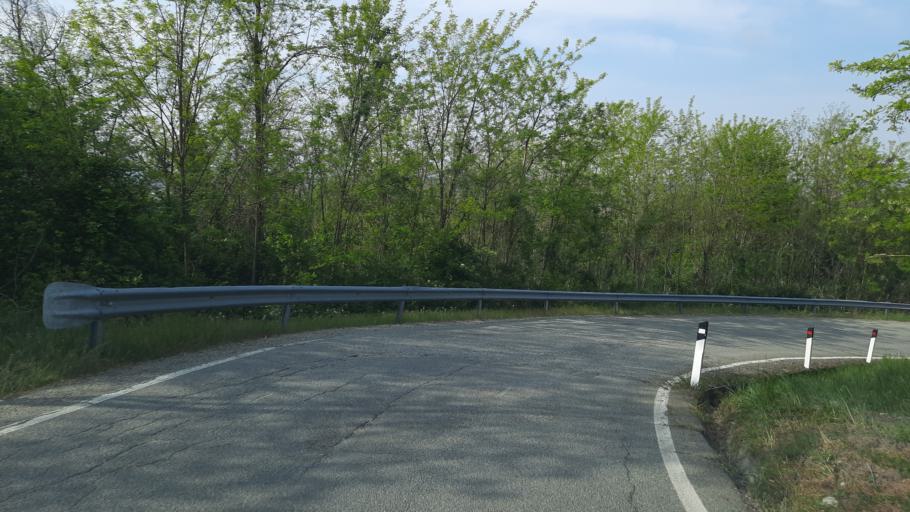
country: IT
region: Piedmont
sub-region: Provincia di Vercelli
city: Palazzolo Vercellese
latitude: 45.1751
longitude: 8.2648
